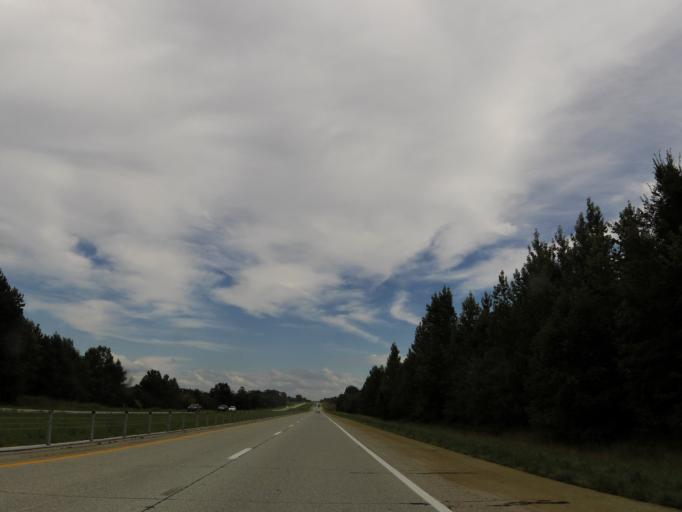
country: US
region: Kentucky
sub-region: Caldwell County
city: Princeton
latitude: 36.9818
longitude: -87.9150
